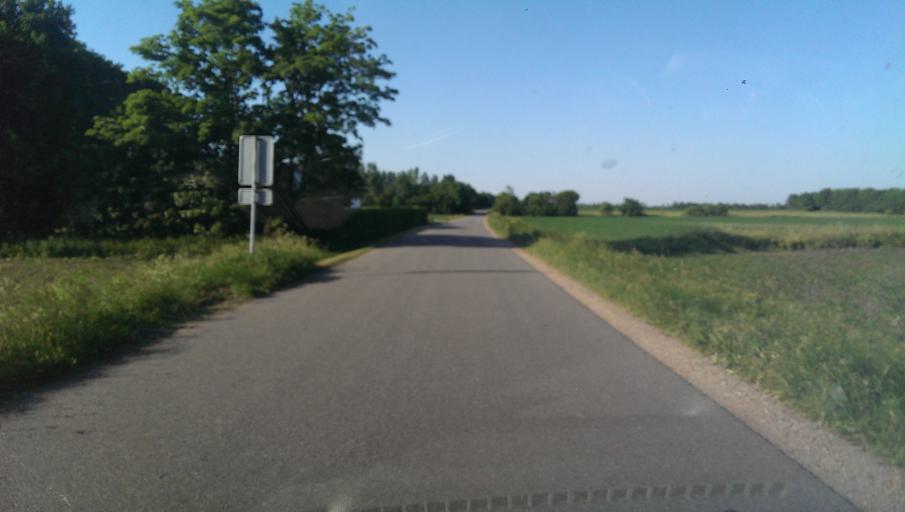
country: DK
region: South Denmark
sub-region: Esbjerg Kommune
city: Bramming
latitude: 55.5466
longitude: 8.7046
